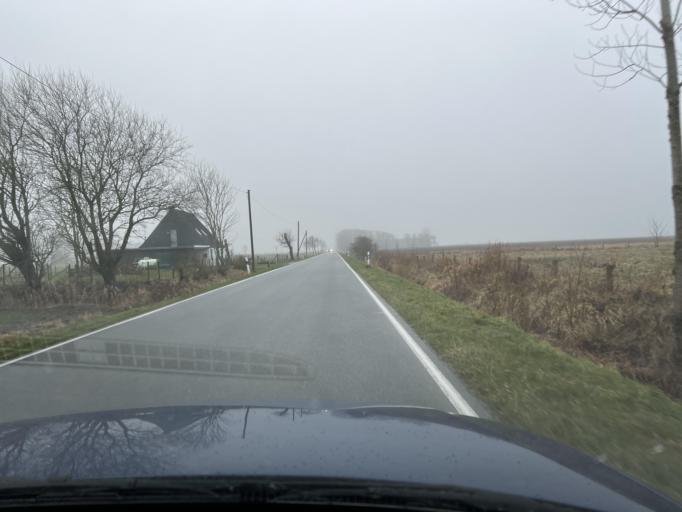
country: DE
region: Schleswig-Holstein
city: Wesselburenerkoog
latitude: 54.2527
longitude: 8.9035
